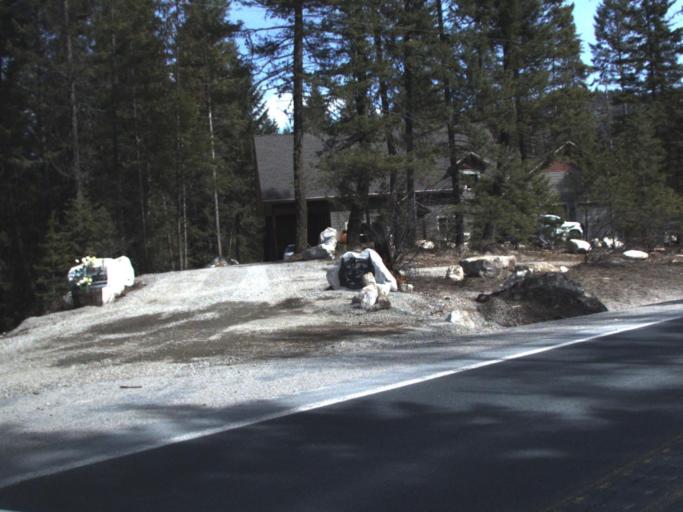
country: US
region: Washington
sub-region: Stevens County
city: Chewelah
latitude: 48.5278
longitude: -117.6365
